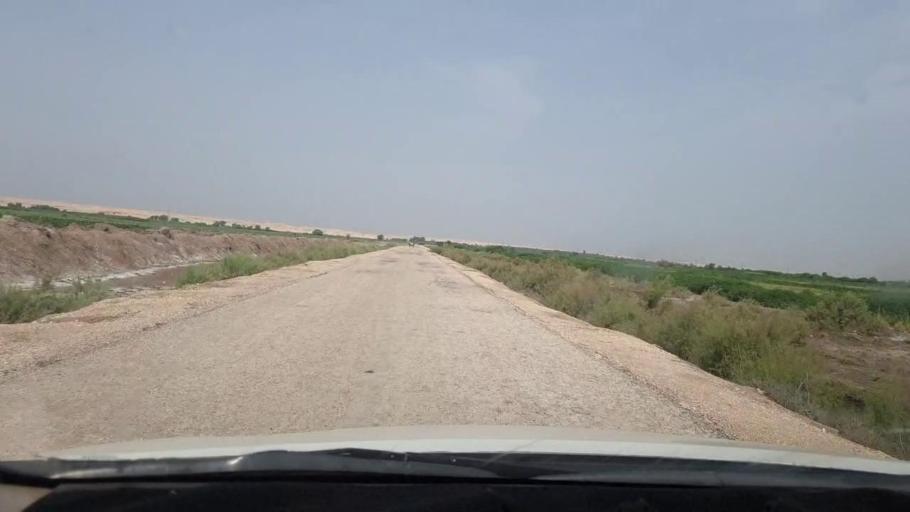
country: PK
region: Sindh
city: Rohri
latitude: 27.5949
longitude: 68.9981
